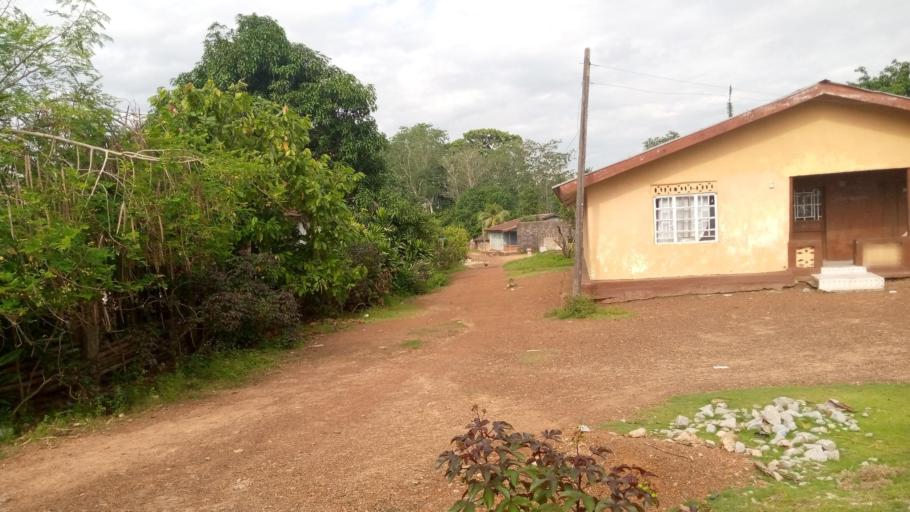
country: SL
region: Southern Province
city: Pujehun
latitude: 7.3503
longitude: -11.7191
